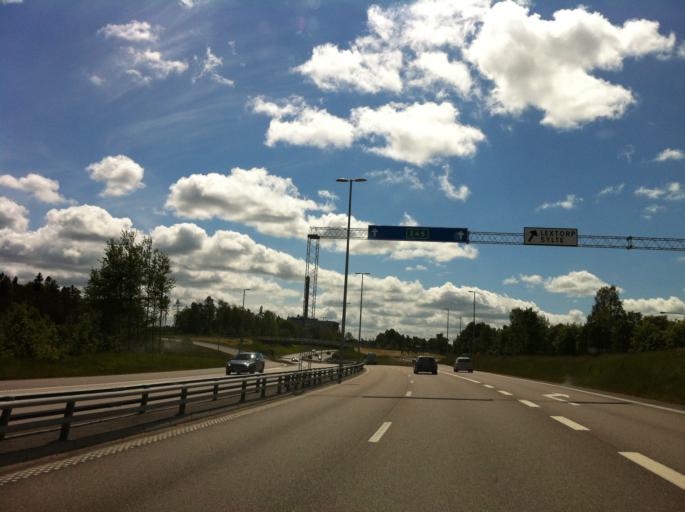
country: SE
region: Vaestra Goetaland
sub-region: Trollhattan
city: Trollhattan
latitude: 58.2594
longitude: 12.2849
